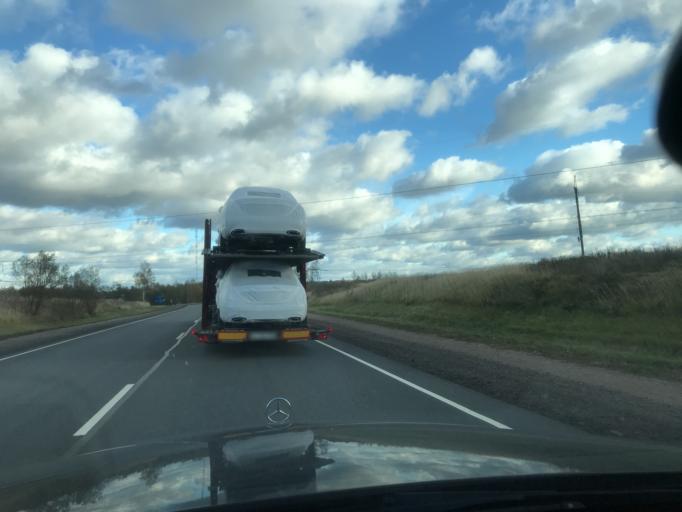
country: RU
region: Pskov
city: Novosokol'niki
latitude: 56.3226
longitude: 30.1186
